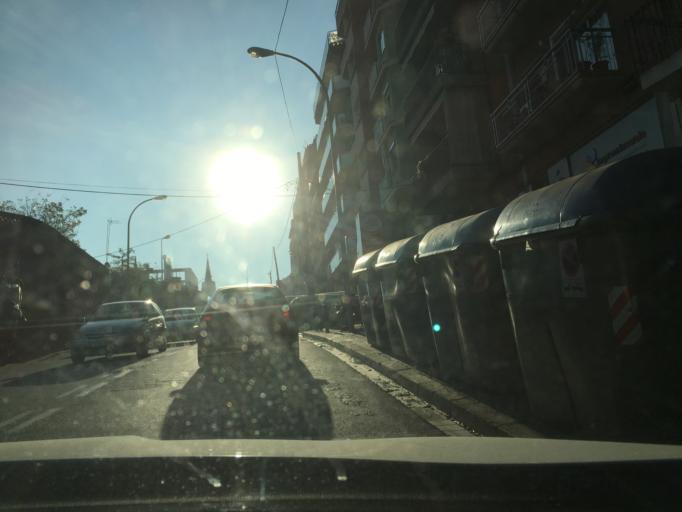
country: ES
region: Catalonia
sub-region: Provincia de Barcelona
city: Santa Coloma de Gramenet
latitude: 41.4551
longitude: 2.2100
